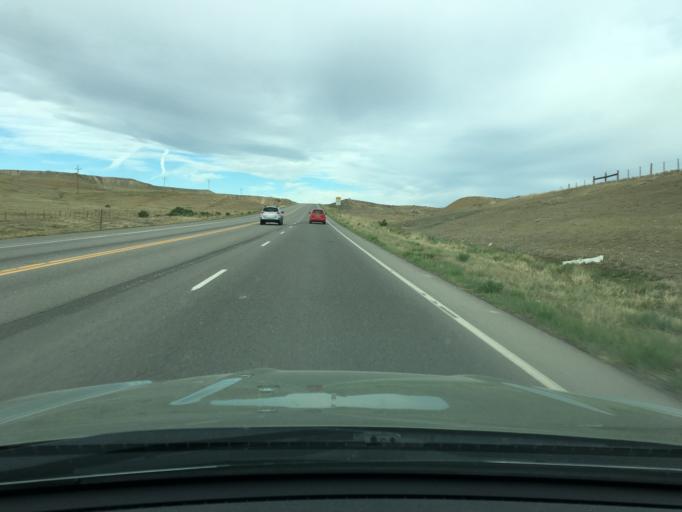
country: US
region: Colorado
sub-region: Delta County
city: Orchard City
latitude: 38.7978
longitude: -107.8425
